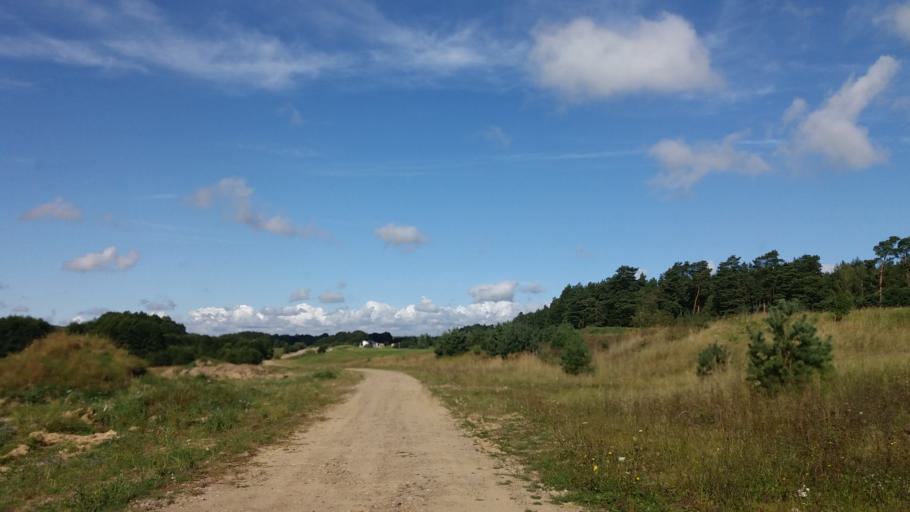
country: PL
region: West Pomeranian Voivodeship
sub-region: Powiat choszczenski
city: Krzecin
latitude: 53.1301
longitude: 15.4986
